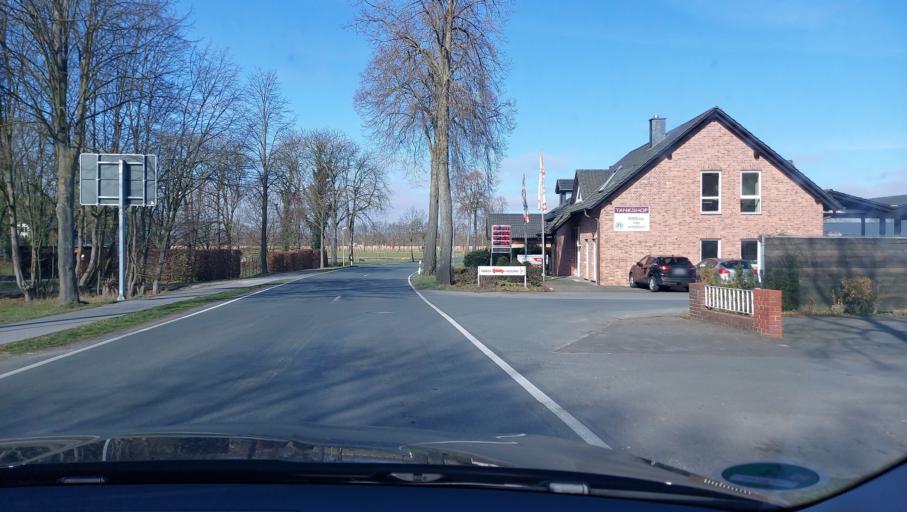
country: DE
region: North Rhine-Westphalia
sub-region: Regierungsbezirk Detmold
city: Verl
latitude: 51.9193
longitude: 8.4518
